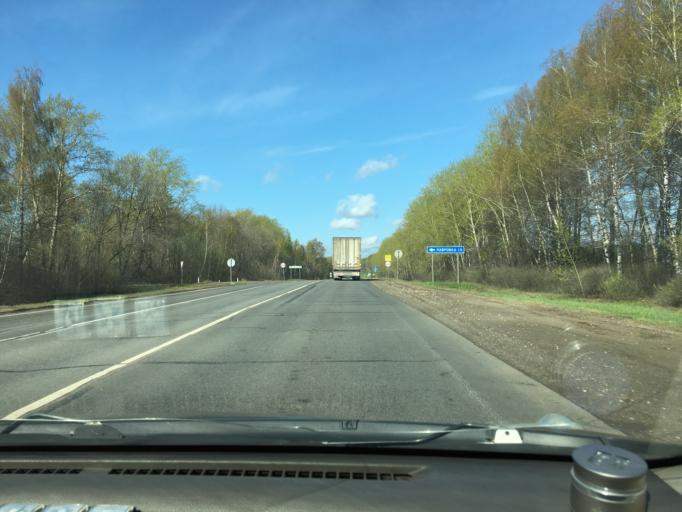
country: RU
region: Nizjnij Novgorod
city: Pamyat' Parizhskoy Kommuny
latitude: 56.0277
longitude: 44.5661
